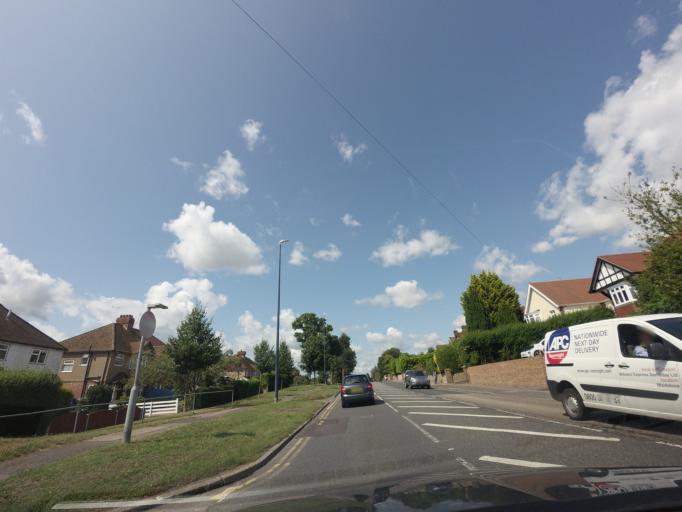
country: GB
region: England
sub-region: Kent
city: Boxley
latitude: 51.2677
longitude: 0.5711
